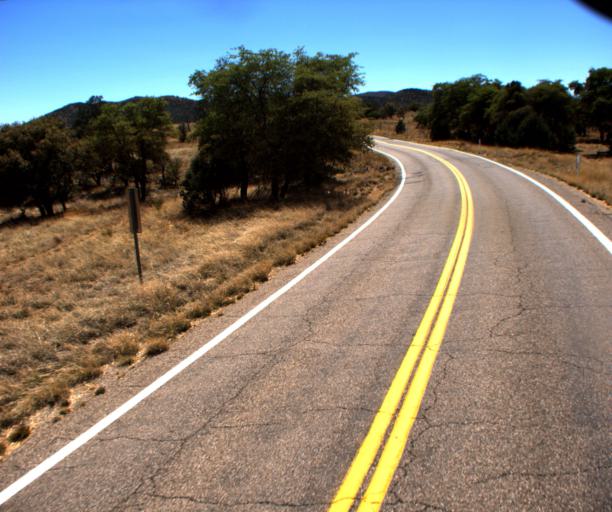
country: US
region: Arizona
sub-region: Cochise County
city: Huachuca City
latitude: 31.5730
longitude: -110.5577
